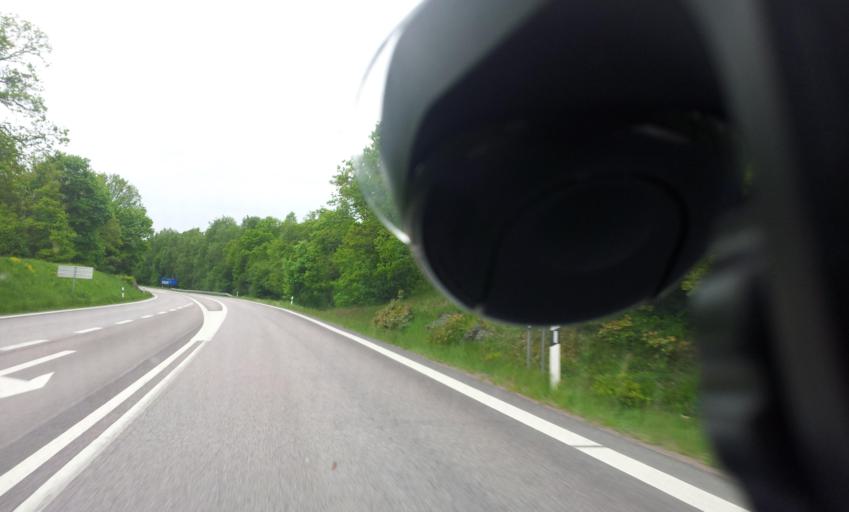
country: SE
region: Kalmar
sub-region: Monsteras Kommun
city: Moensteras
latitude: 57.0580
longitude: 16.4416
